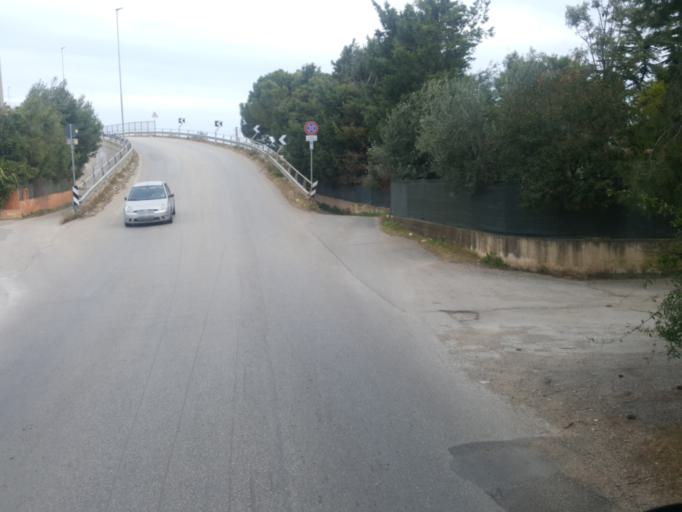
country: IT
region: Apulia
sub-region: Provincia di Barletta - Andria - Trani
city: Bisceglie
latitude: 41.2219
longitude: 16.5053
